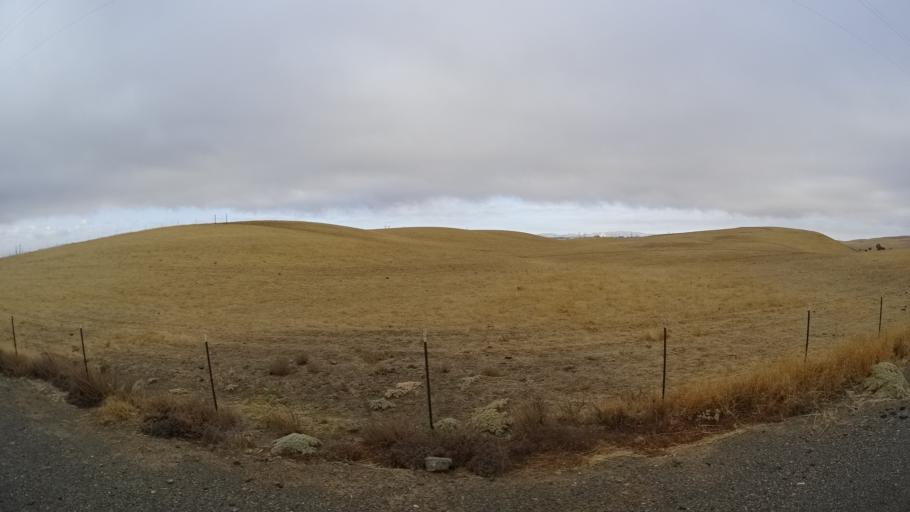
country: US
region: California
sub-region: Yolo County
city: Dunnigan
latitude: 38.8445
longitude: -122.0438
